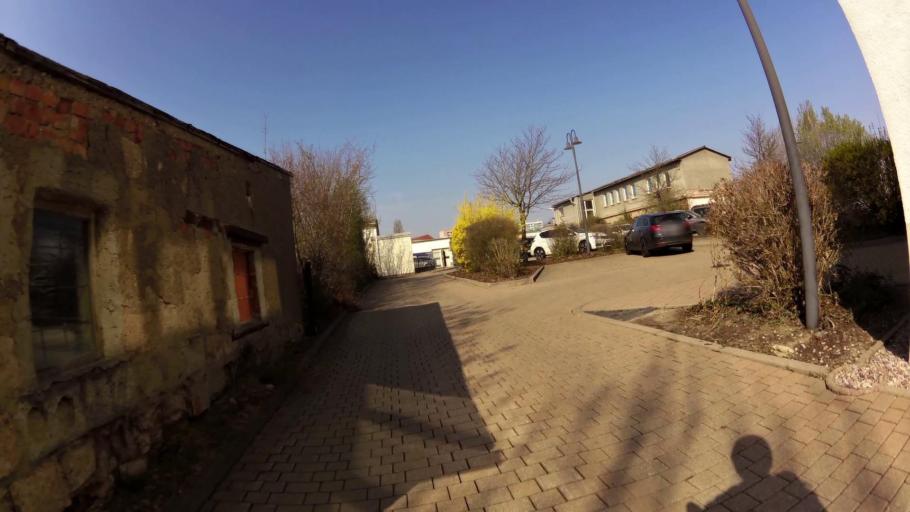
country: DE
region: Thuringia
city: Weimar
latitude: 50.9948
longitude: 11.3244
